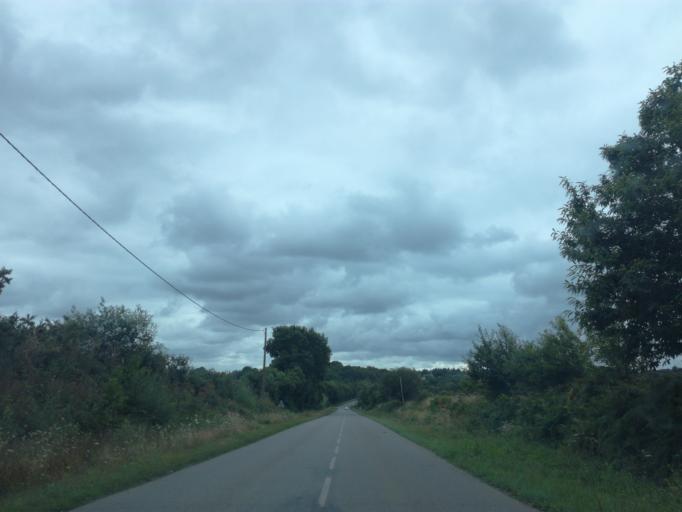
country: FR
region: Brittany
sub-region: Departement du Morbihan
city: Cleguerec
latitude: 48.1119
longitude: -3.0419
